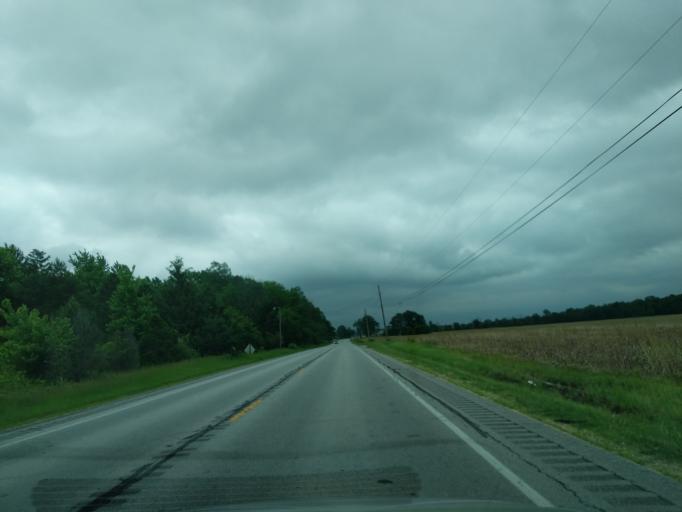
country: US
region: Indiana
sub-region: Madison County
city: Frankton
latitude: 40.2775
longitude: -85.7440
